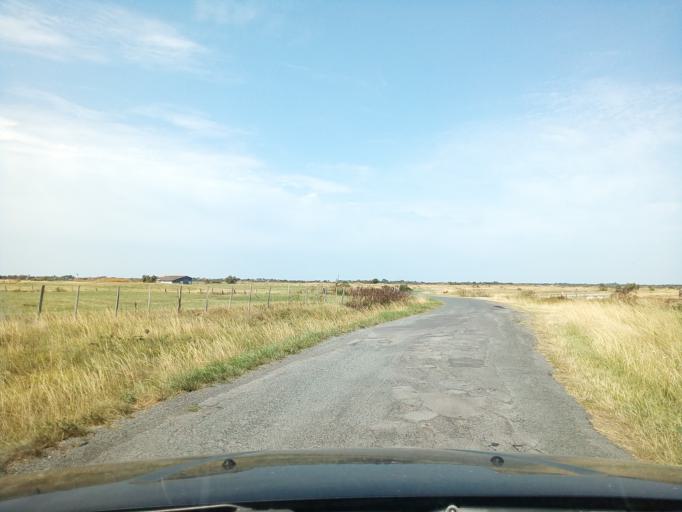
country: FR
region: Poitou-Charentes
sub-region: Departement de la Charente-Maritime
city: Boyard-Ville
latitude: 45.9522
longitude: -1.2710
